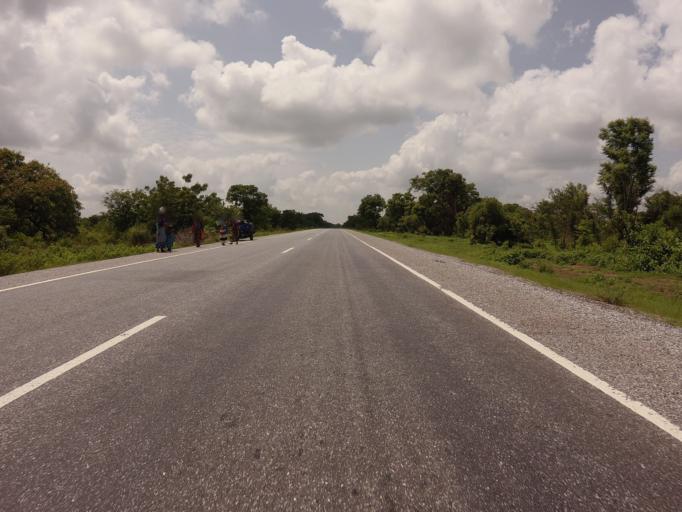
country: GH
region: Northern
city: Tamale
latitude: 9.1503
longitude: -1.3867
